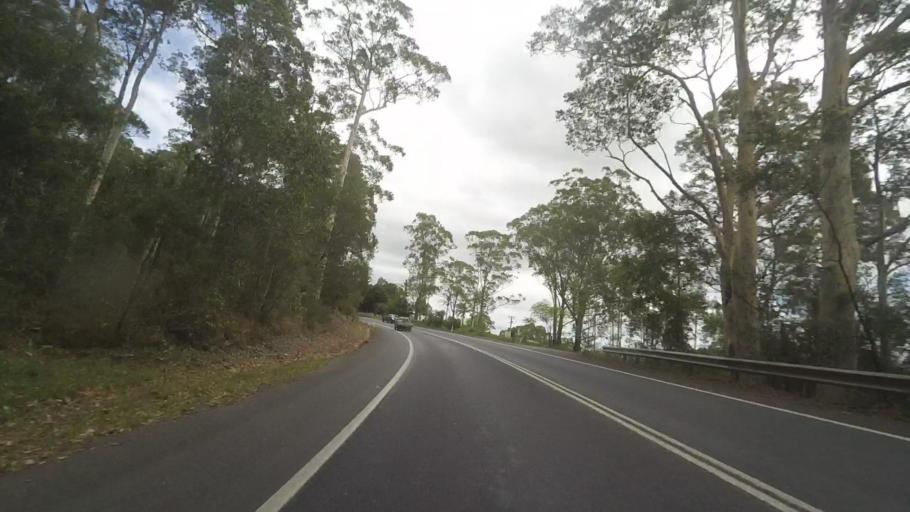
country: AU
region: New South Wales
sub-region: Shoalhaven Shire
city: Falls Creek
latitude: -35.0810
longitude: 150.5190
